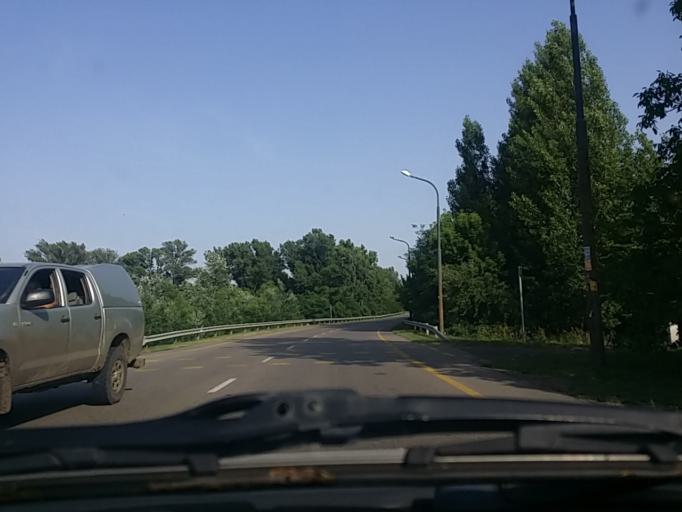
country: HU
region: Jasz-Nagykun-Szolnok
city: Jaszbereny
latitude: 47.4903
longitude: 19.8802
